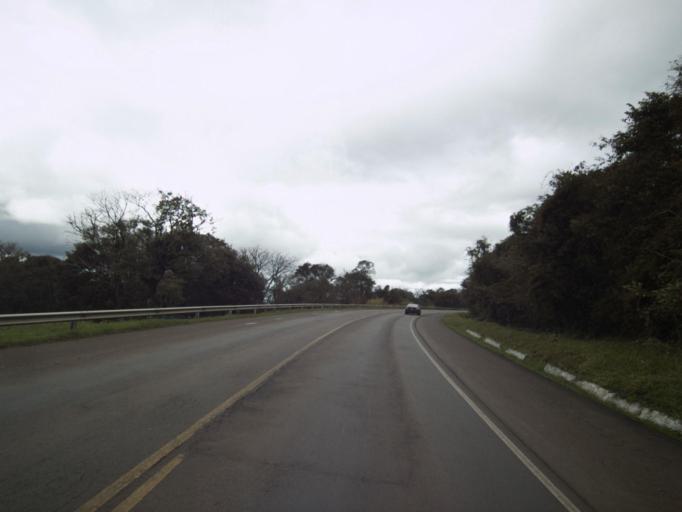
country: BR
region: Santa Catarina
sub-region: Concordia
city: Concordia
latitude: -27.2607
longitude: -51.9540
